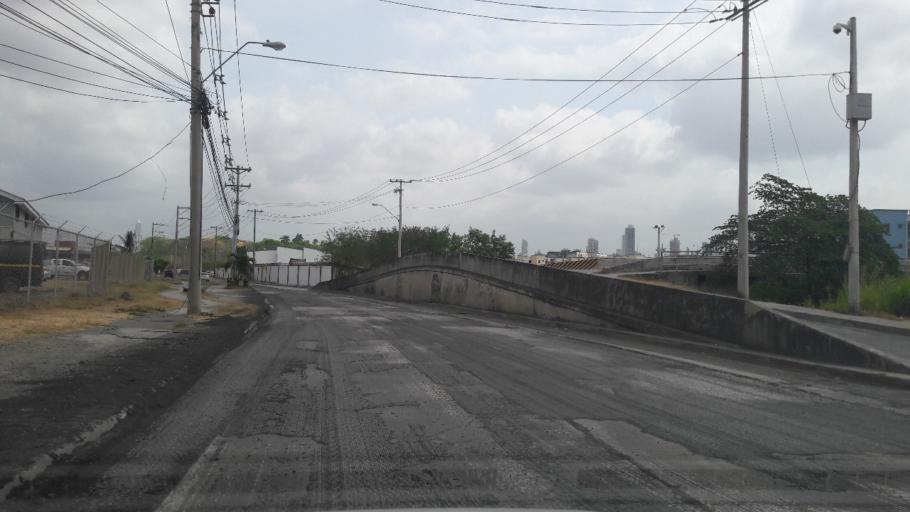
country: PA
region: Panama
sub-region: Distrito de Panama
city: Ancon
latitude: 8.9687
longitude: -79.5478
